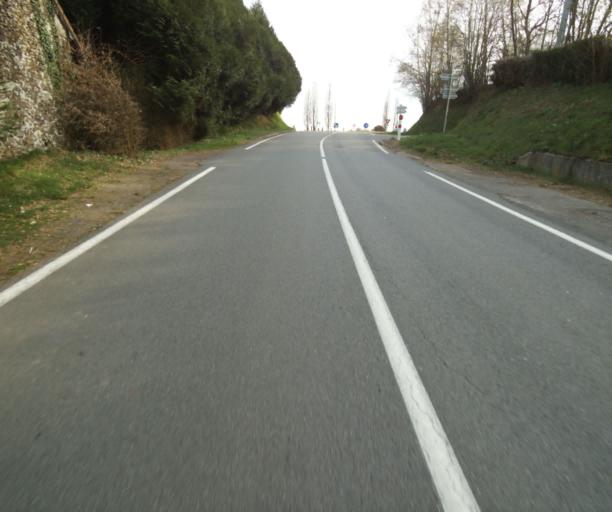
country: FR
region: Limousin
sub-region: Departement de la Correze
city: Naves
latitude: 45.3285
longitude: 1.7692
